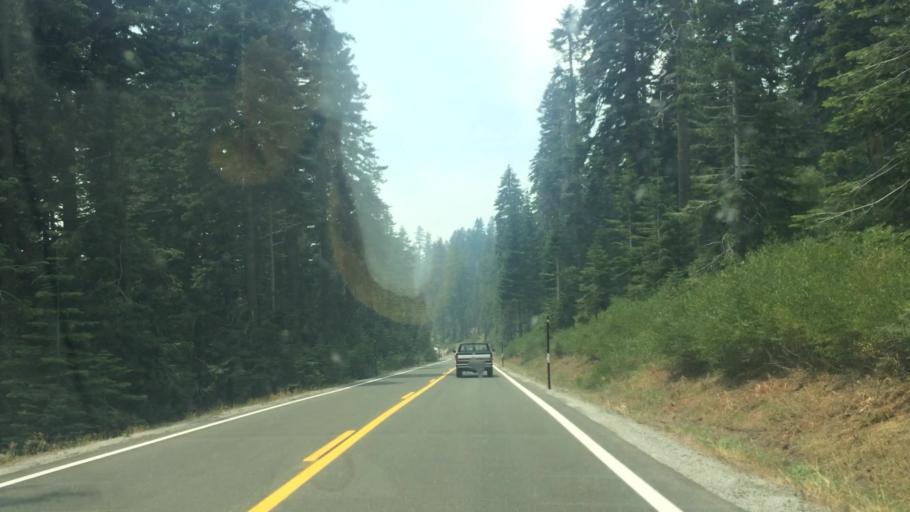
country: US
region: California
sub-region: Calaveras County
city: Arnold
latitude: 38.5794
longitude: -120.2572
